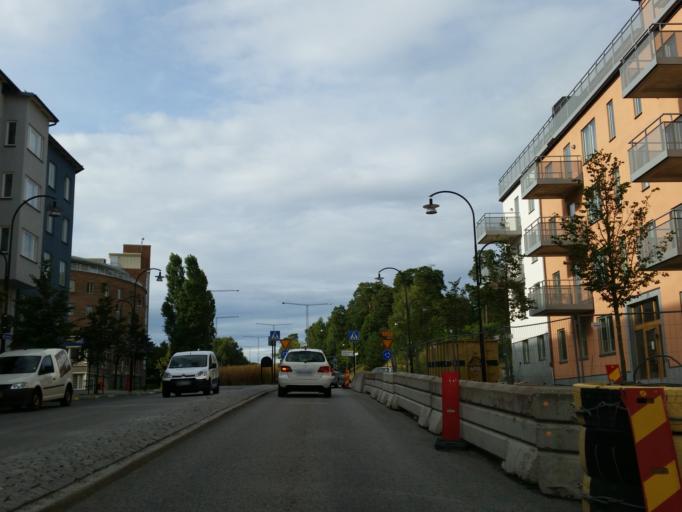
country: SE
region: Stockholm
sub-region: Sollentuna Kommun
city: Sollentuna
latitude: 59.4300
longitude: 17.9515
